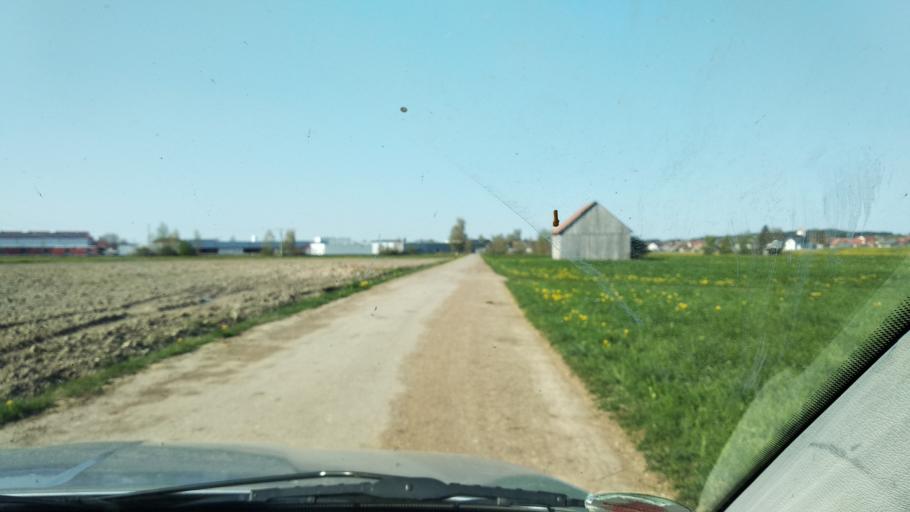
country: DE
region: Bavaria
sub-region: Swabia
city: Hawangen
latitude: 47.9629
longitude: 10.2586
